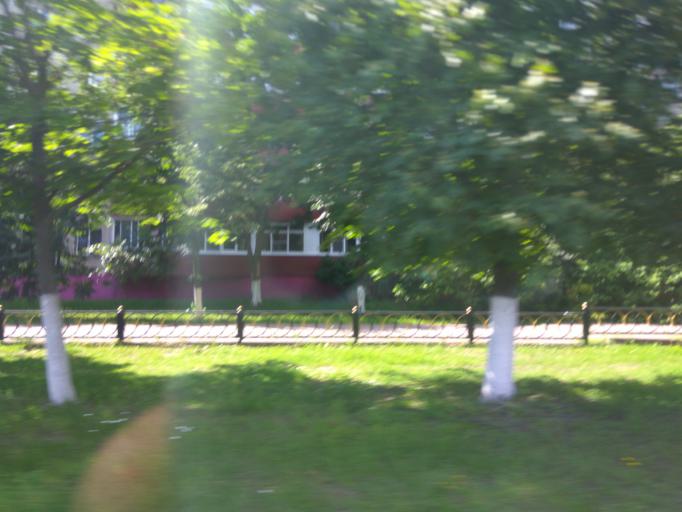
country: RU
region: Moskovskaya
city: Ramenskoye
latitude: 55.5676
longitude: 38.2362
